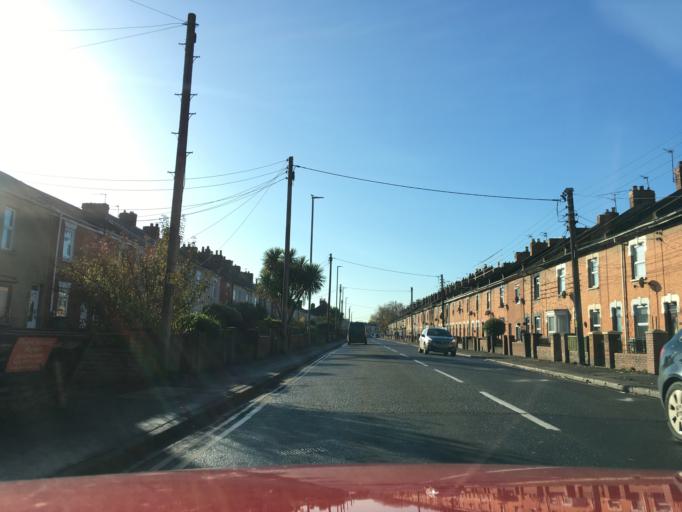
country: GB
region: England
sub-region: Somerset
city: Bridgwater
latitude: 51.1344
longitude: -2.9942
